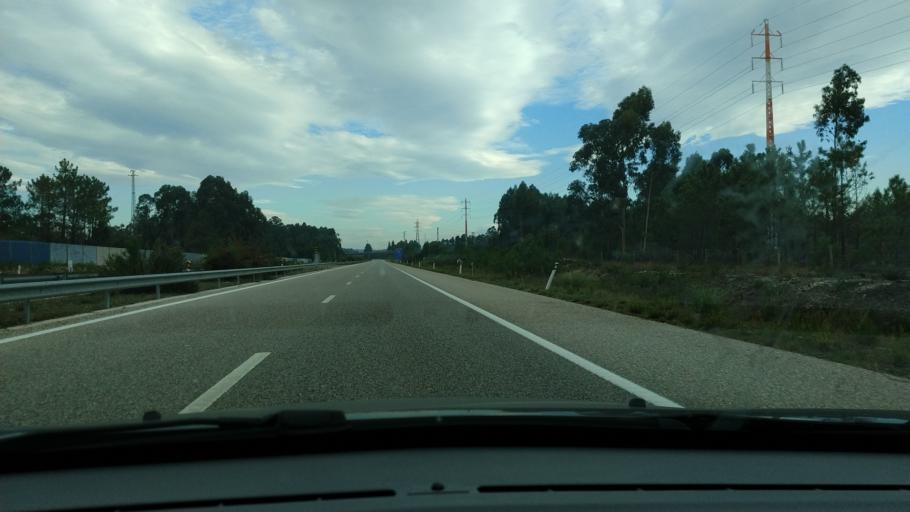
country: PT
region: Coimbra
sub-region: Mira
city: Mira
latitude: 40.4800
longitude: -8.6868
